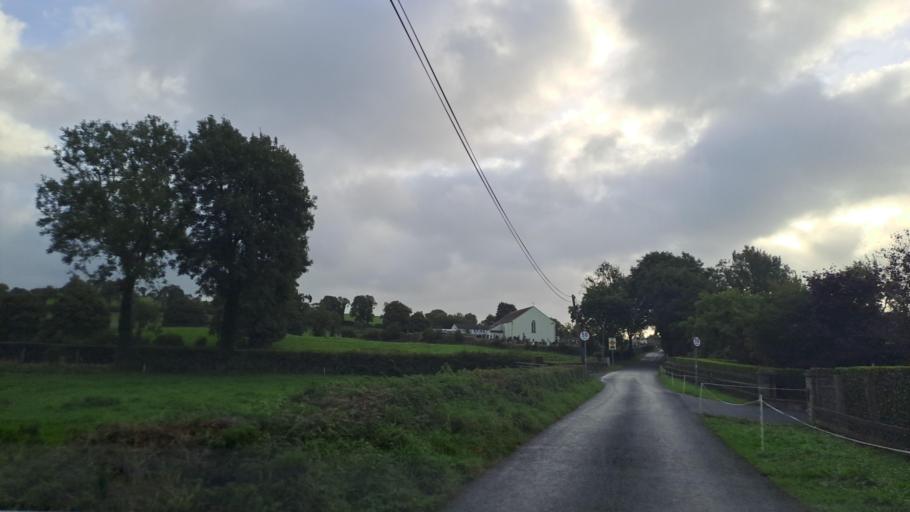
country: IE
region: Ulster
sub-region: An Cabhan
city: Kingscourt
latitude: 53.9532
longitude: -6.7826
